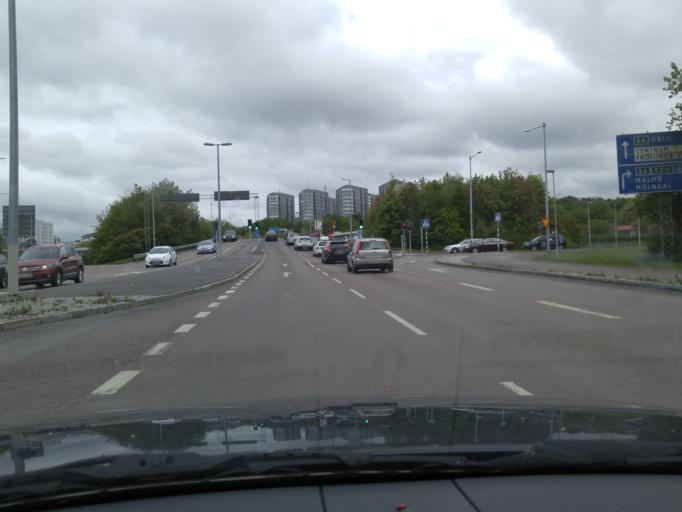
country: SE
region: Vaestra Goetaland
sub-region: Goteborg
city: Majorna
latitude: 57.6465
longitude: 11.9173
